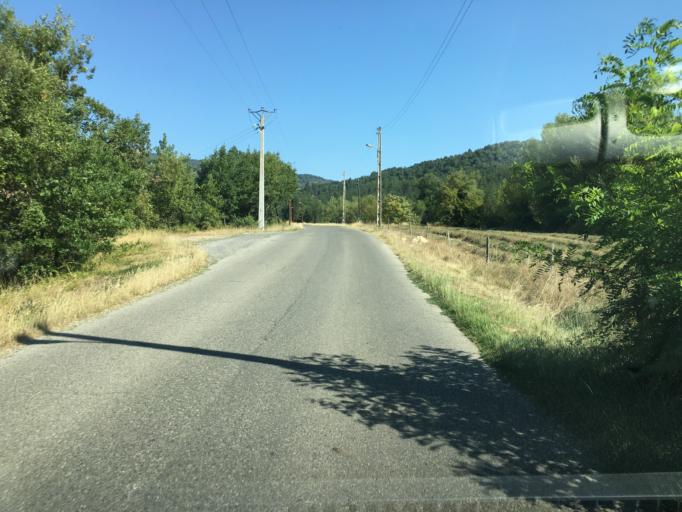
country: FR
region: Provence-Alpes-Cote d'Azur
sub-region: Departement des Alpes-de-Haute-Provence
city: Mallemoisson
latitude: 44.0548
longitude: 6.1489
